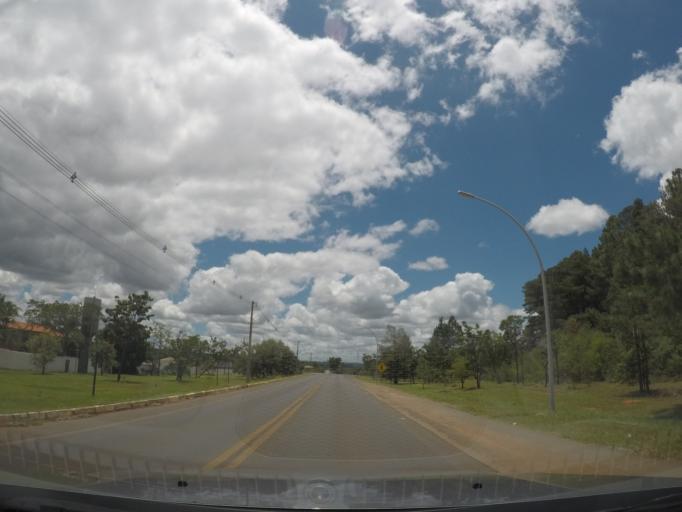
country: BR
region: Federal District
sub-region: Brasilia
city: Brasilia
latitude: -15.7839
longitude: -47.7988
